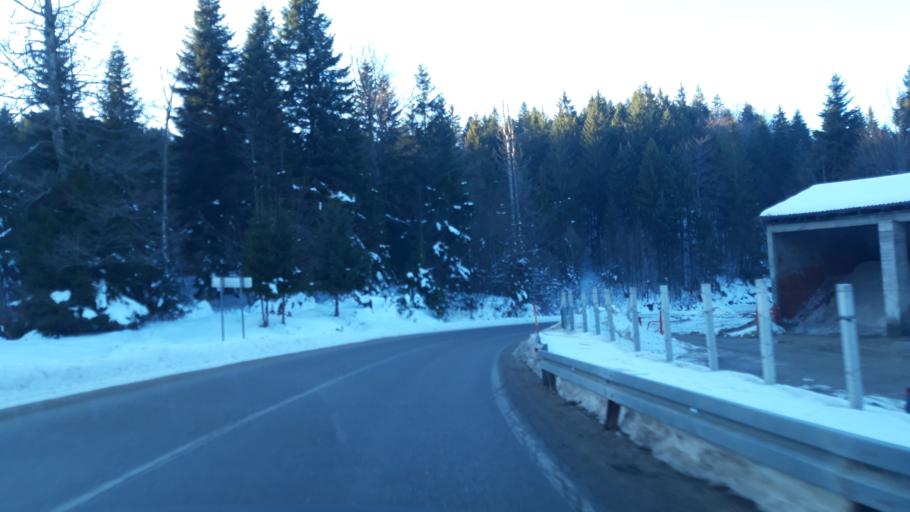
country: BA
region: Republika Srpska
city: Vlasenica
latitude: 44.1452
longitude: 18.9401
